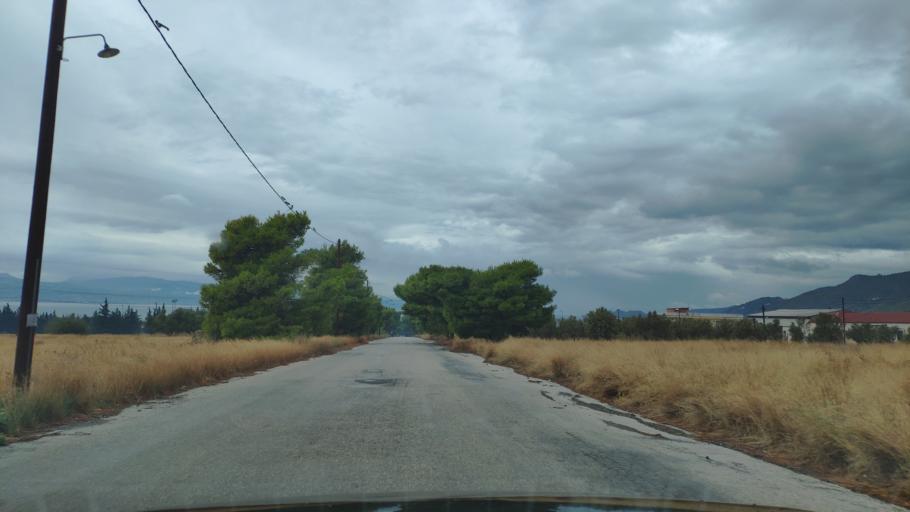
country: GR
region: Peloponnese
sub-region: Nomos Korinthias
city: Loutraki
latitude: 37.9656
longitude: 22.9899
